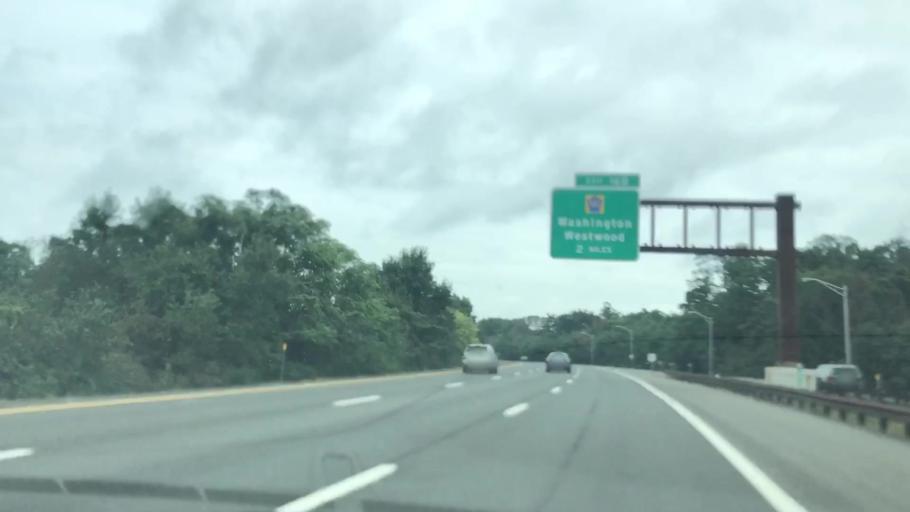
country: US
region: New Jersey
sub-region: Bergen County
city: Paramus
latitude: 40.9671
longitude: -74.0646
